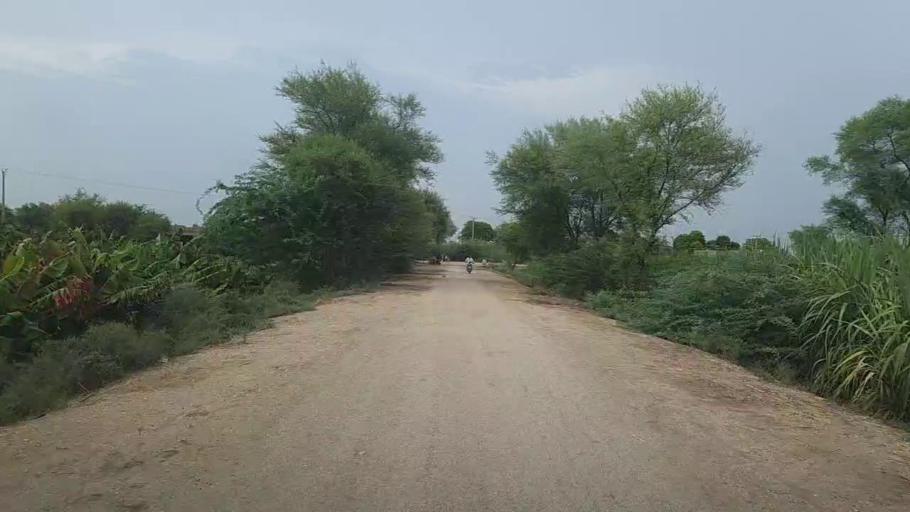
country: PK
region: Sindh
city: Karaundi
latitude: 26.9829
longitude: 68.4339
